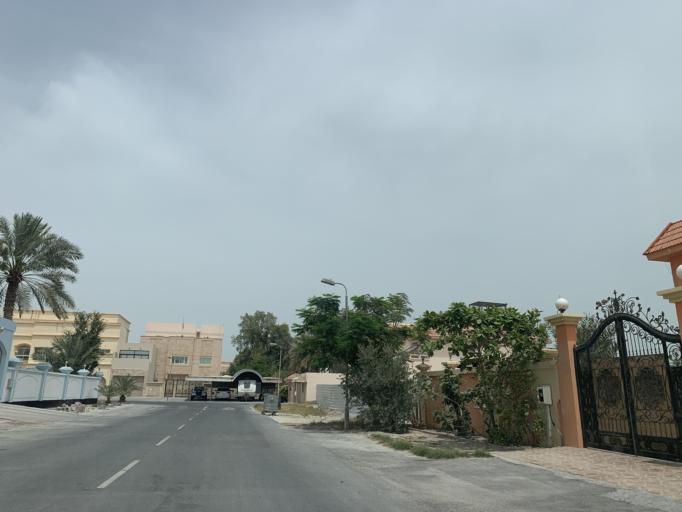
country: BH
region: Northern
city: Ar Rifa'
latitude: 26.1359
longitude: 50.5678
